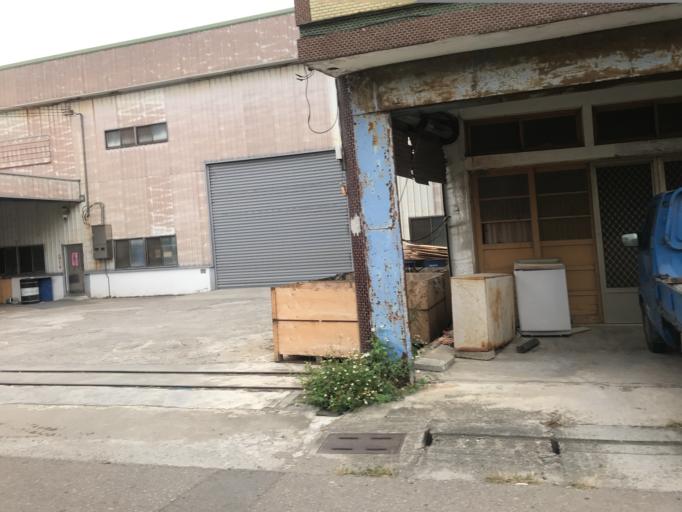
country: TW
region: Taiwan
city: Fengyuan
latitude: 24.3532
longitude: 120.6123
